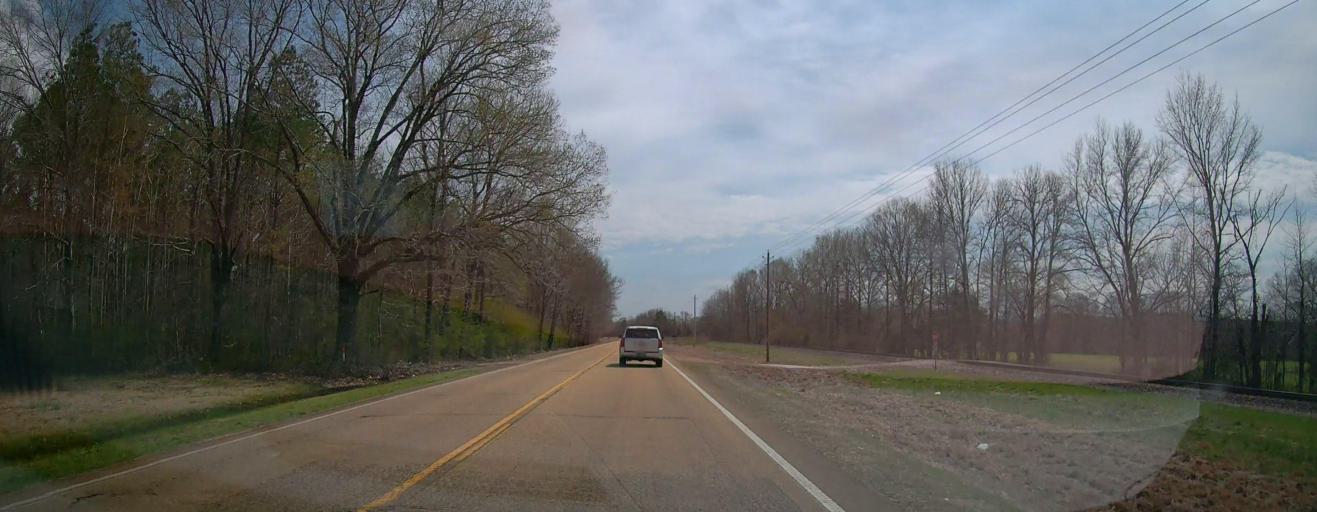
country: US
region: Mississippi
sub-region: Benton County
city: Ashland
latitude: 34.6280
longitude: -89.2637
